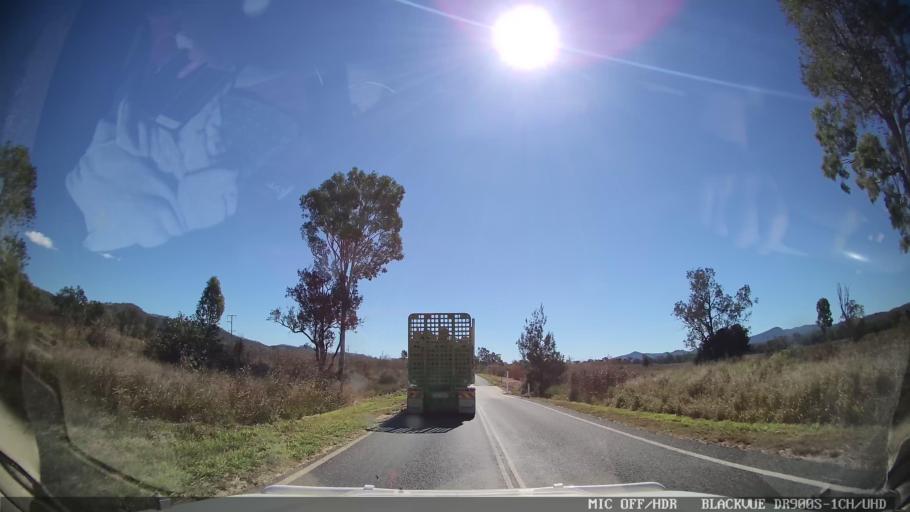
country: AU
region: Queensland
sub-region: Gladstone
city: Toolooa
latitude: -24.2724
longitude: 151.2757
